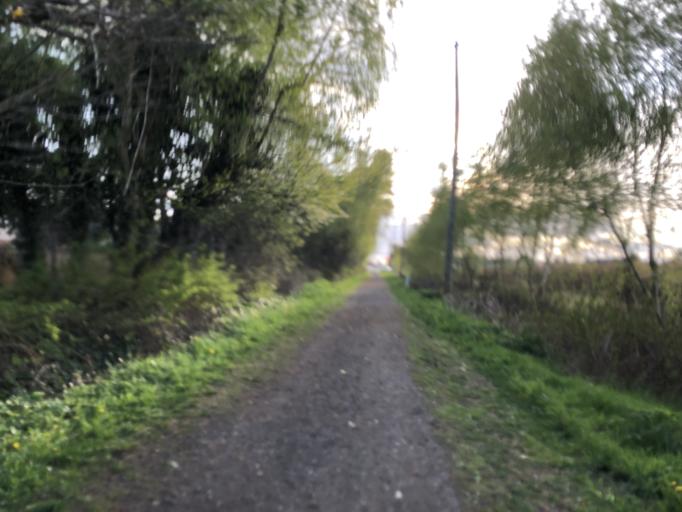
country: CA
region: British Columbia
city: Richmond
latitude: 49.1480
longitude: -123.1102
